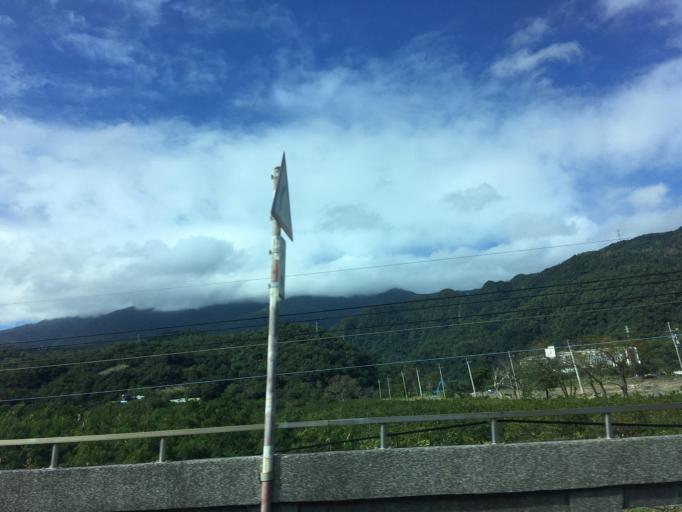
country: TW
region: Taiwan
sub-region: Yilan
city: Yilan
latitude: 24.8221
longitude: 121.7596
